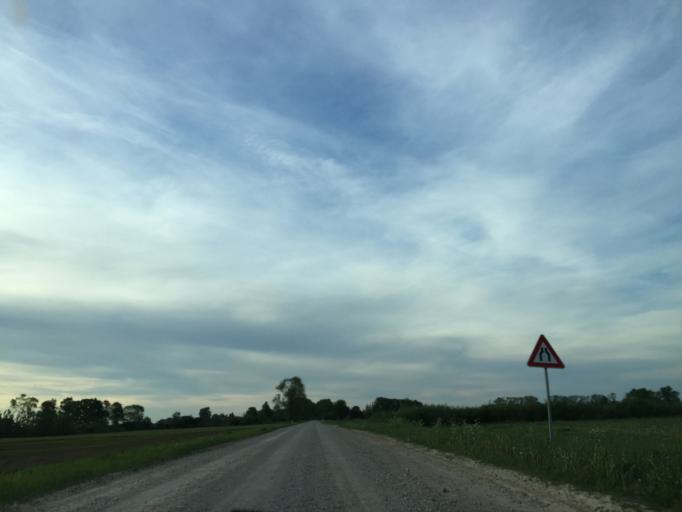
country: LV
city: Tireli
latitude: 56.7011
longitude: 23.4990
